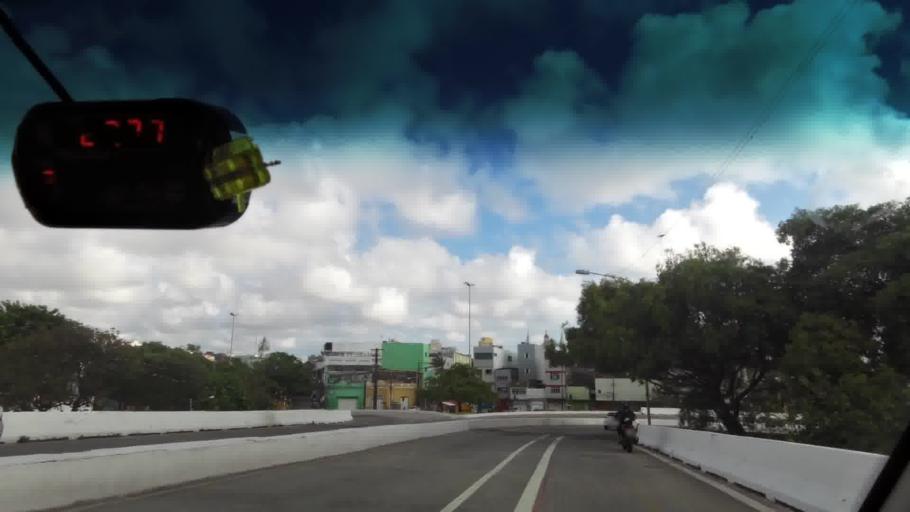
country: BR
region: Pernambuco
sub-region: Recife
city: Recife
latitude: -8.0721
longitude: -34.8801
